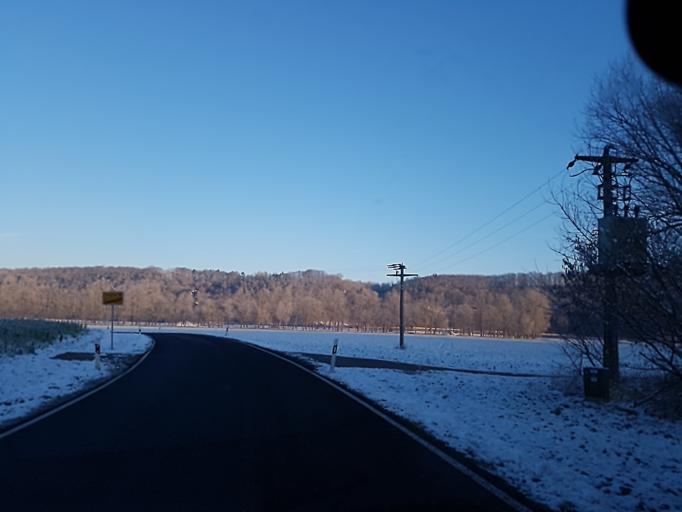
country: DE
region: Saxony
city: Leisnig
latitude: 51.1533
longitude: 12.9713
